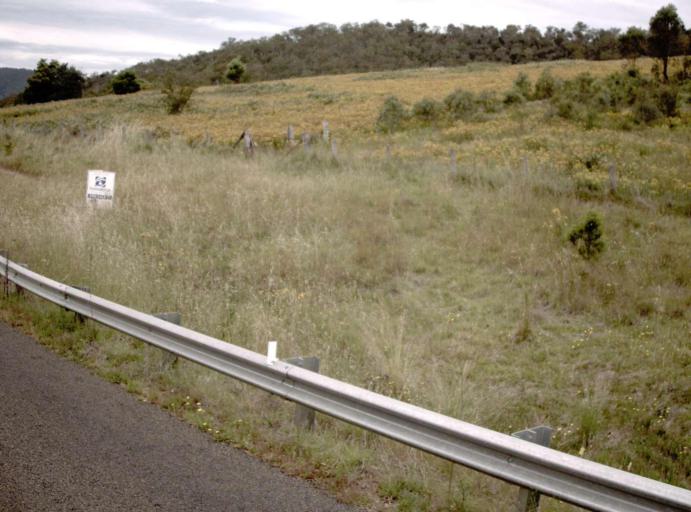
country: AU
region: Victoria
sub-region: East Gippsland
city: Bairnsdale
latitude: -37.4736
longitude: 147.2230
